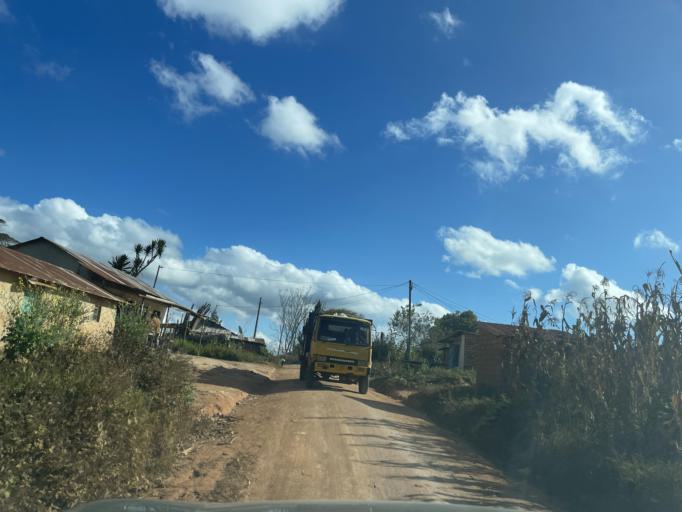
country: TZ
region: Iringa
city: Makungu
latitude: -8.4729
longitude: 35.4197
